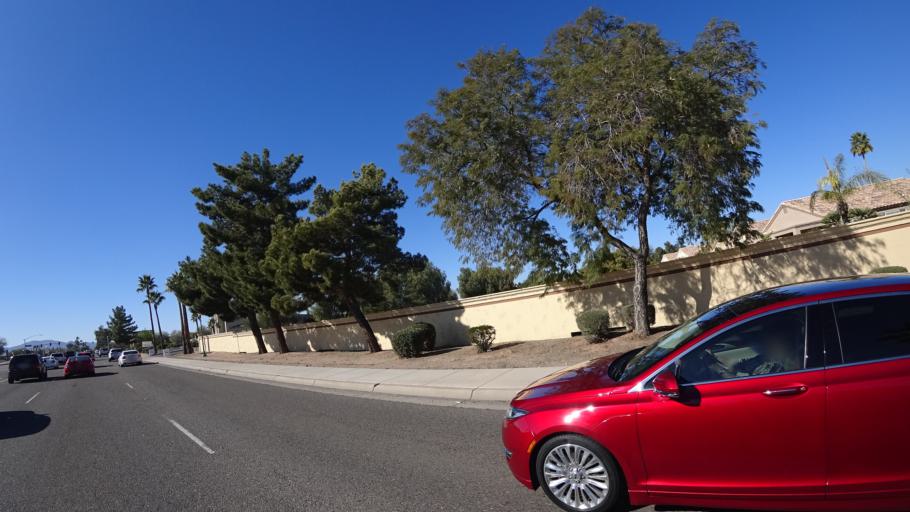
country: US
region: Arizona
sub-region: Maricopa County
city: Sun City West
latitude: 33.6387
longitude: -112.3740
